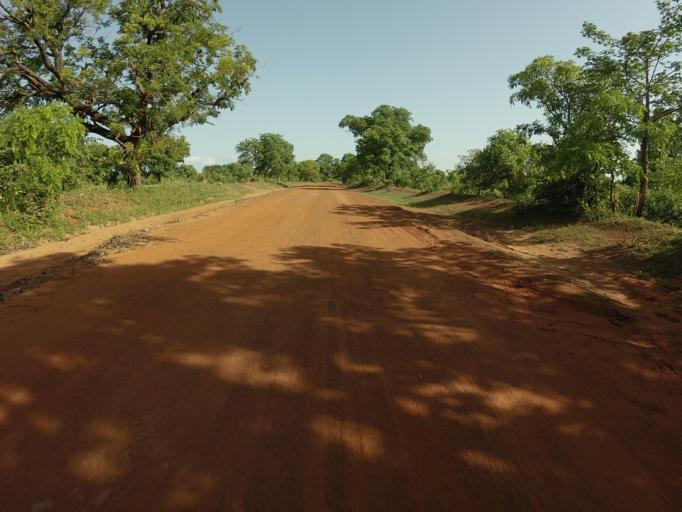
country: GH
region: Upper East
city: Bawku
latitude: 10.7411
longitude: -0.2003
